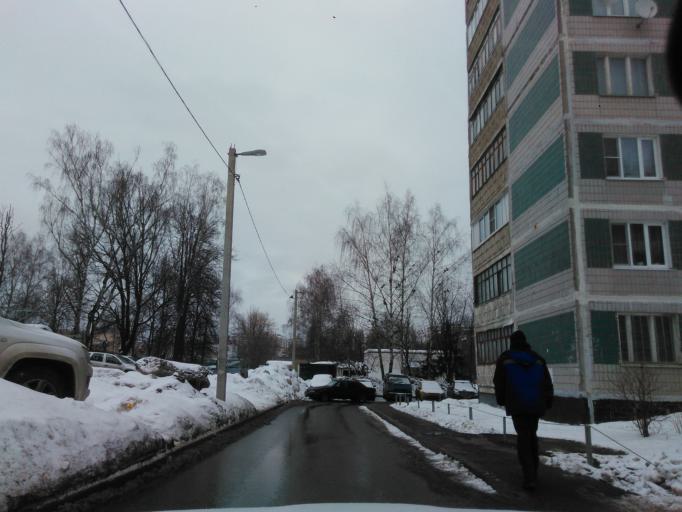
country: RU
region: Moskovskaya
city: Andreyevka
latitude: 55.9765
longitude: 37.1404
